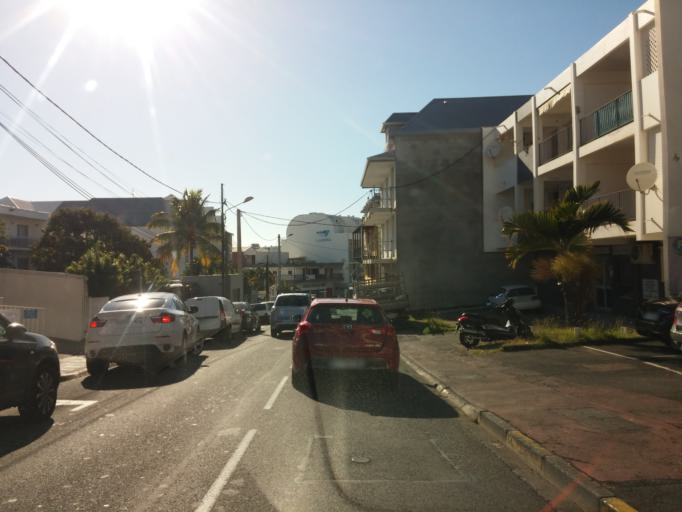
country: RE
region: Reunion
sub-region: Reunion
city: Saint-Denis
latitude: -20.8816
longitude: 55.4552
